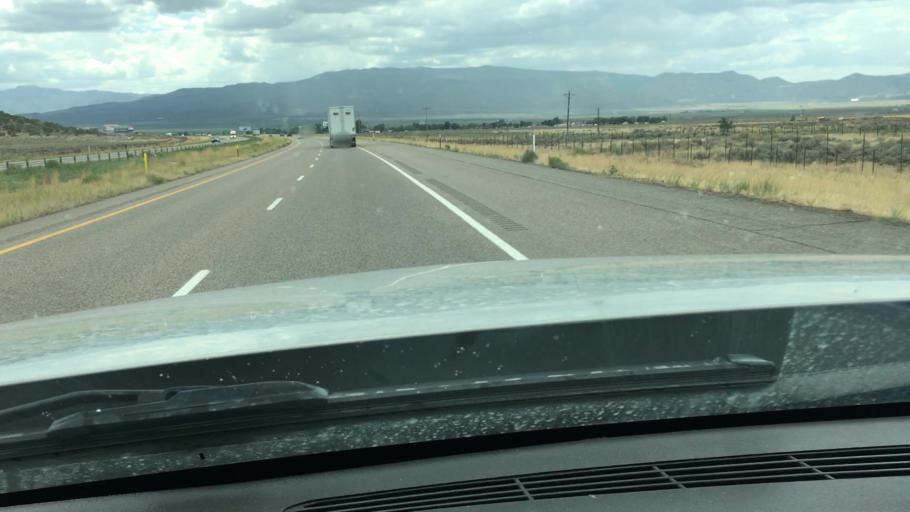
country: US
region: Utah
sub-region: Iron County
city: Cedar City
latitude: 37.6227
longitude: -113.1404
